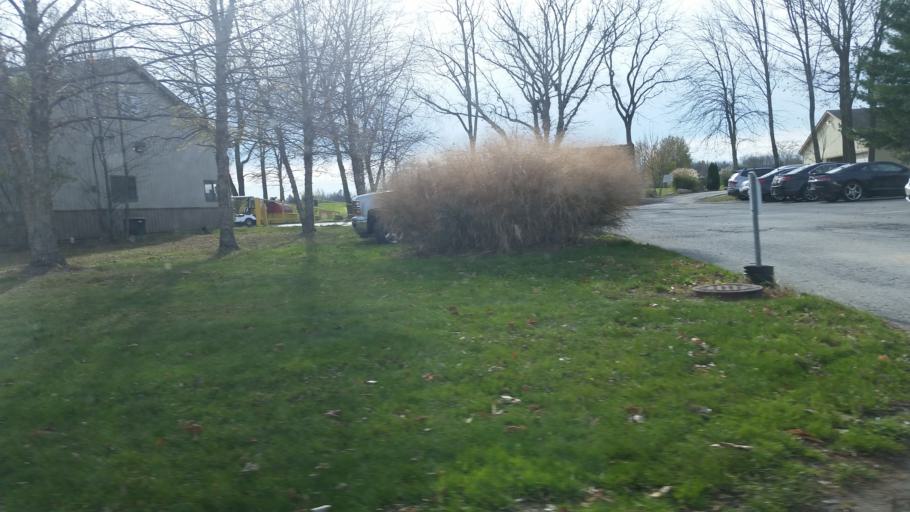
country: US
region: Indiana
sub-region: Howard County
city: Indian Heights
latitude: 40.4261
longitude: -86.1568
